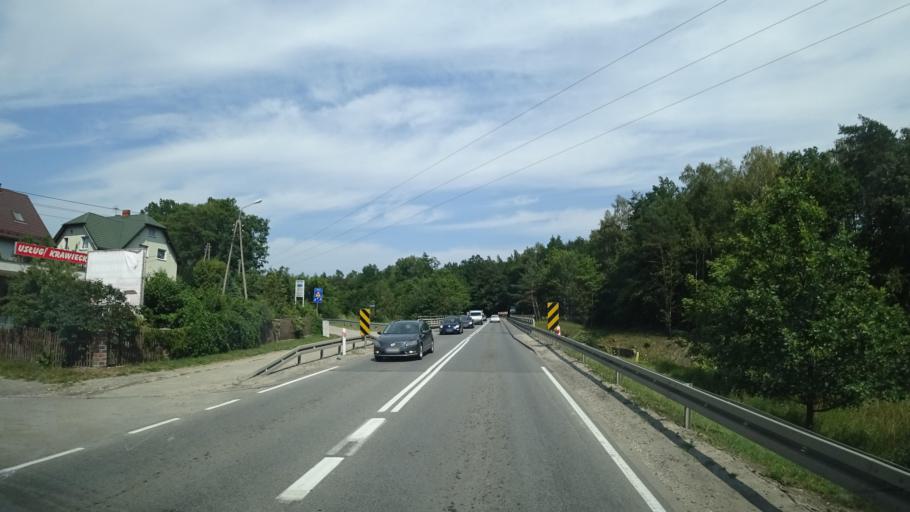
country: PL
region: Pomeranian Voivodeship
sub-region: Powiat kartuski
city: Banino
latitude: 54.3466
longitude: 18.4578
